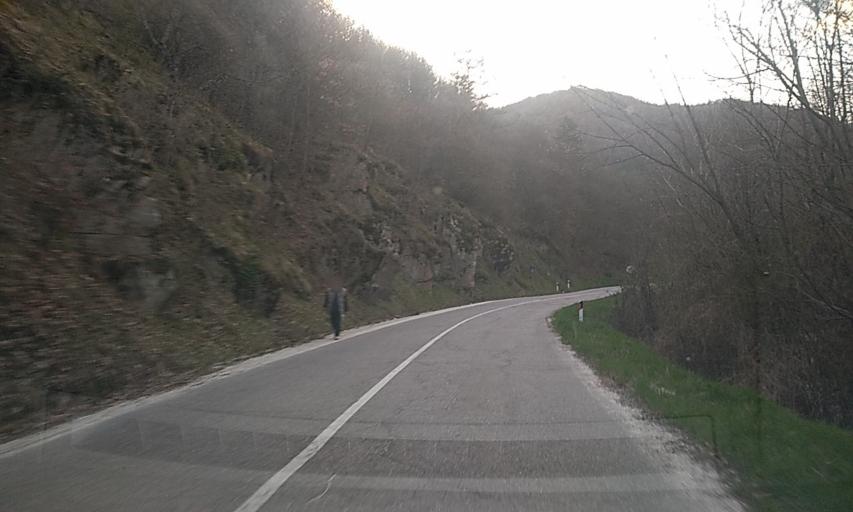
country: RS
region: Central Serbia
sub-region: Pcinjski Okrug
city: Bosilegrad
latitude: 42.4997
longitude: 22.4614
